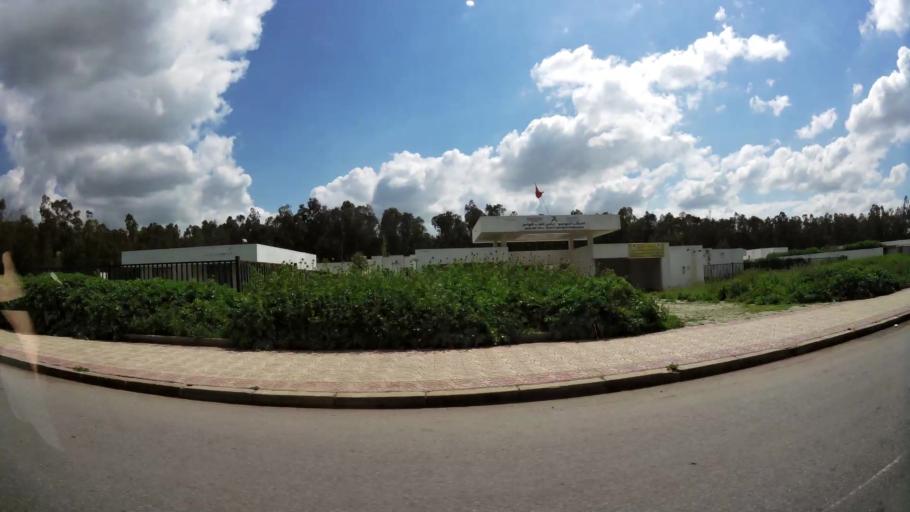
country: MA
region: Chaouia-Ouardigha
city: Nouaseur
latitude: 33.3719
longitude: -7.5449
